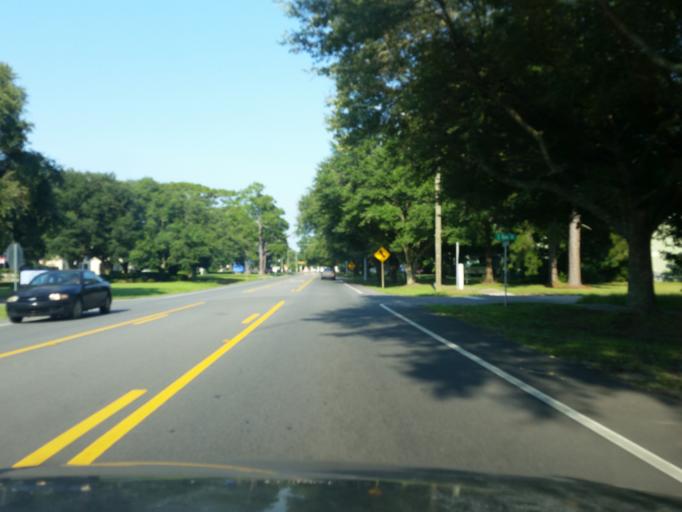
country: US
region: Alabama
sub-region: Baldwin County
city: Foley
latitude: 30.4064
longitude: -87.6788
